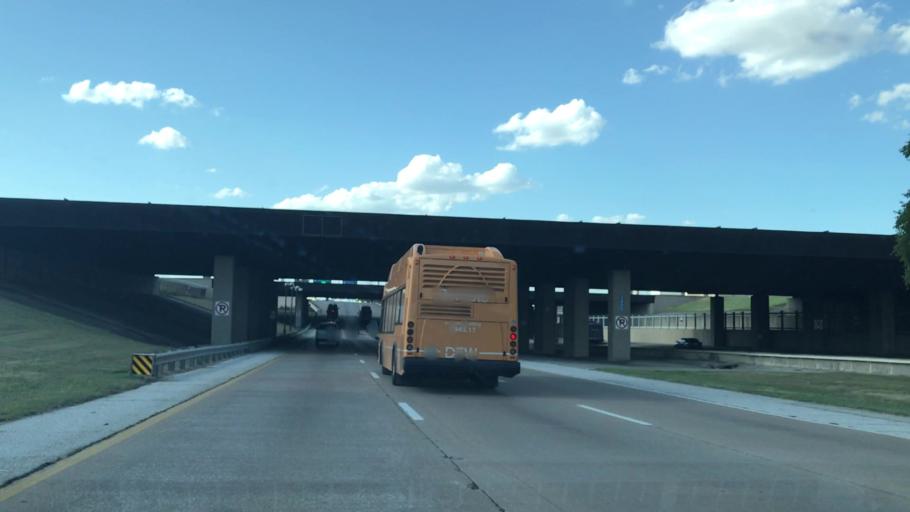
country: US
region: Texas
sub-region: Tarrant County
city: Grapevine
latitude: 32.8843
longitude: -97.0399
